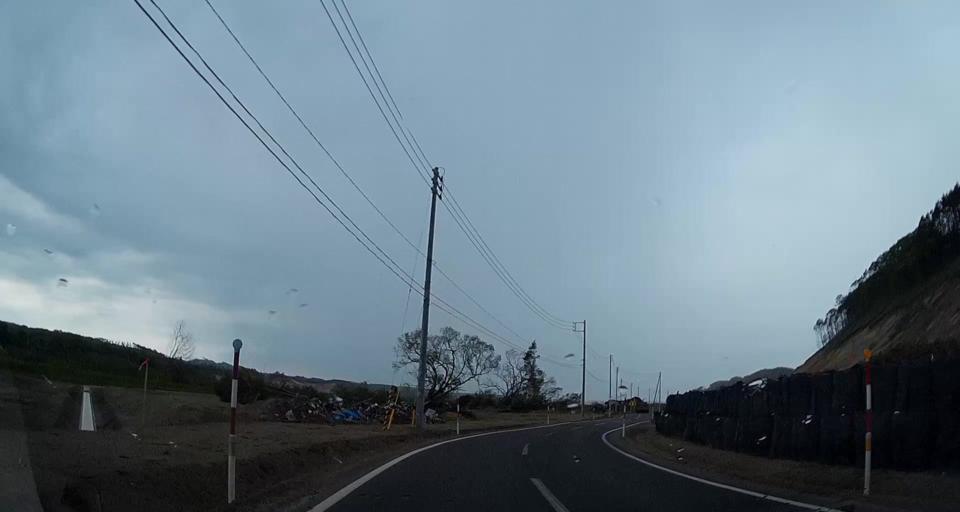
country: JP
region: Hokkaido
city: Chitose
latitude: 42.7536
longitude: 141.9156
